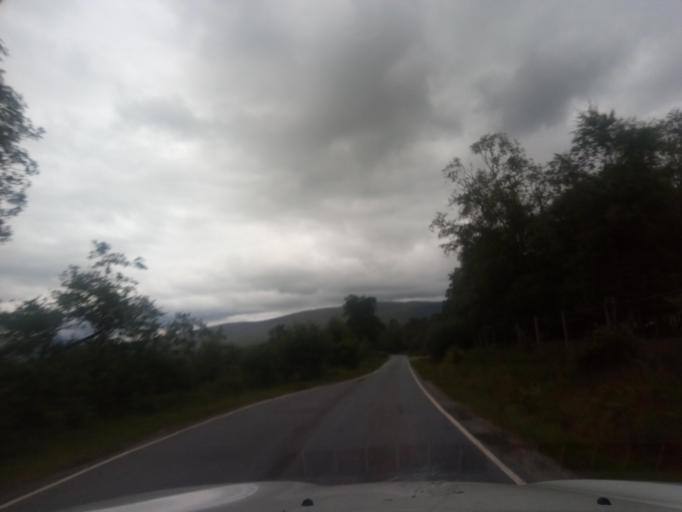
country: GB
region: Scotland
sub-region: Highland
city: Fort William
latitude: 56.8534
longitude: -5.3301
